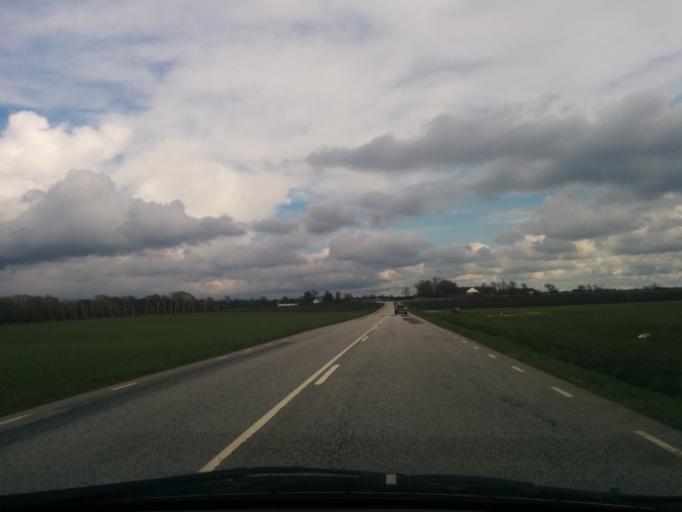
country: SE
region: Skane
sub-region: Svedala Kommun
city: Klagerup
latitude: 55.6363
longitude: 13.2812
